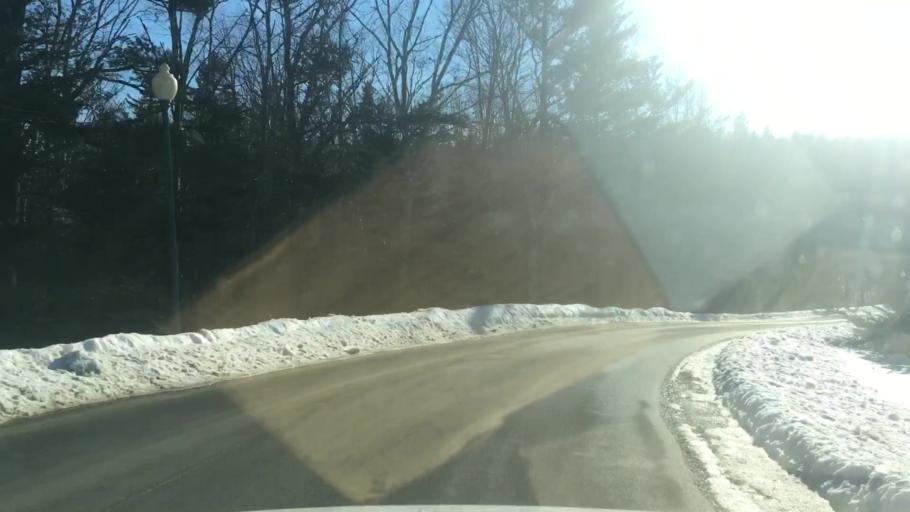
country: US
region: Maine
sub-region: Hancock County
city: Sedgwick
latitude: 44.3892
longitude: -68.5757
